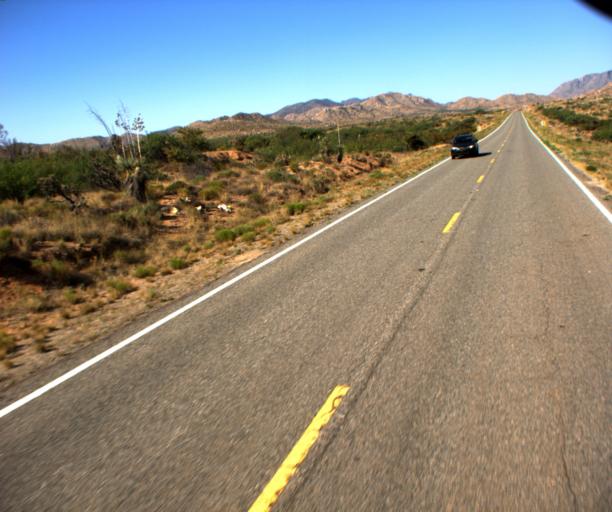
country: US
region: Arizona
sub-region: Graham County
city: Swift Trail Junction
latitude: 32.5874
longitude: -109.6990
